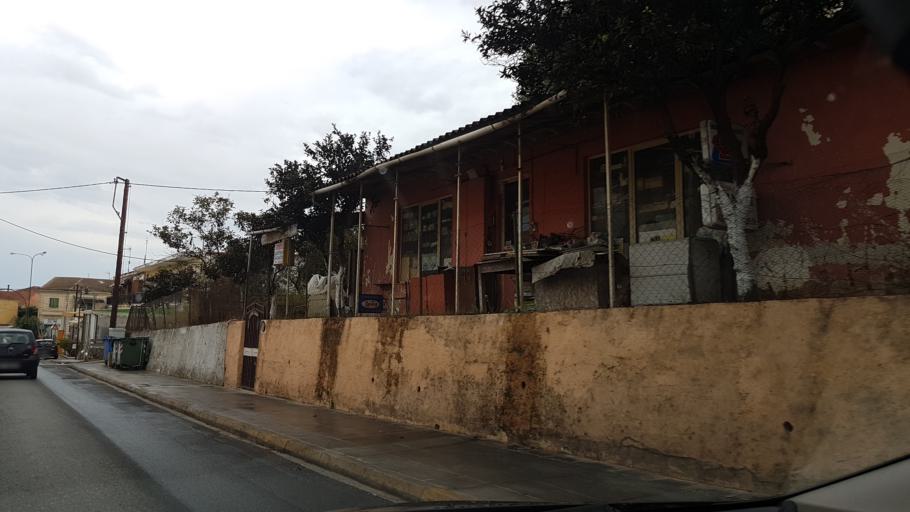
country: GR
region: Ionian Islands
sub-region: Nomos Kerkyras
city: Alepou
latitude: 39.6195
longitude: 19.9074
